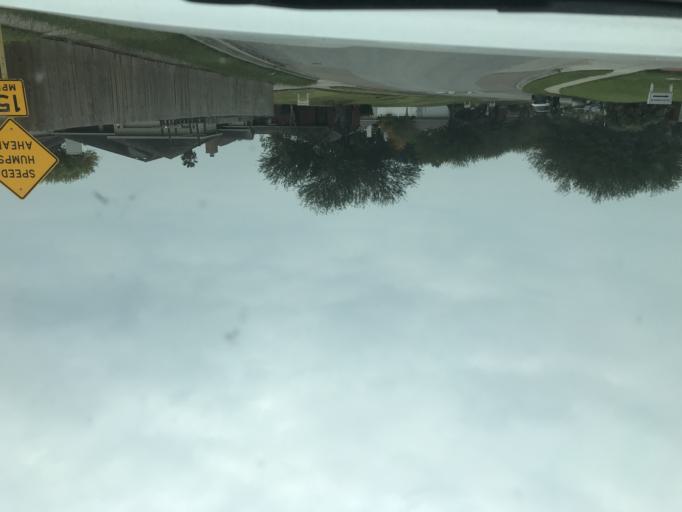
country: US
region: Texas
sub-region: Nueces County
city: Corpus Christi
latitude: 27.6690
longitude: -97.3557
